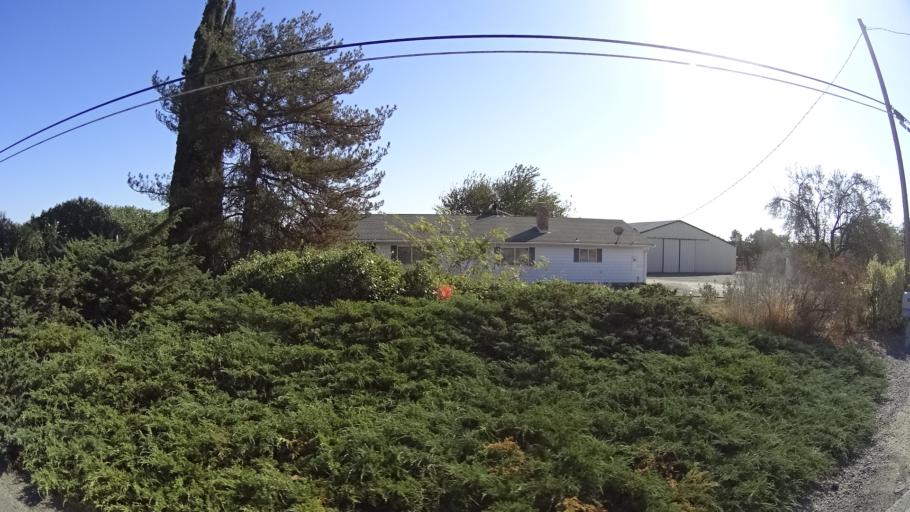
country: US
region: California
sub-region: Yolo County
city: Woodland
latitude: 38.6713
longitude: -121.8703
